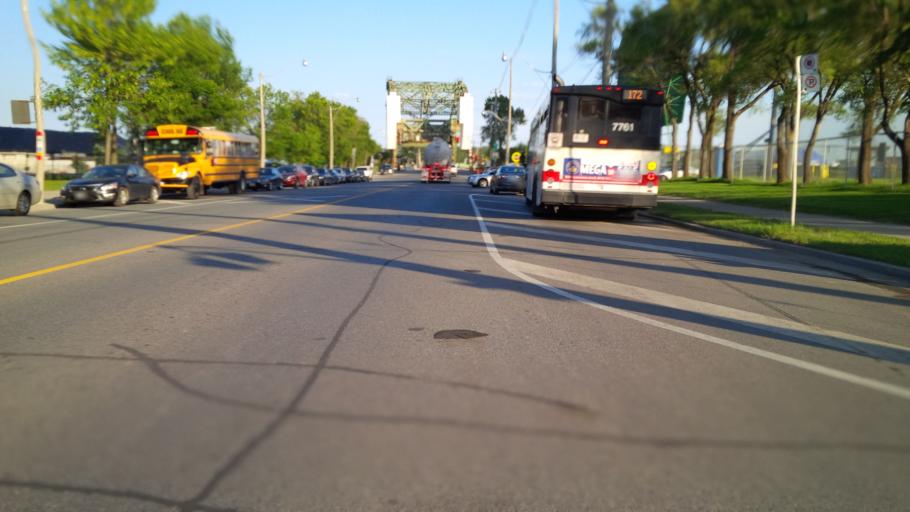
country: CA
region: Ontario
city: Toronto
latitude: 43.6429
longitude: -79.3506
